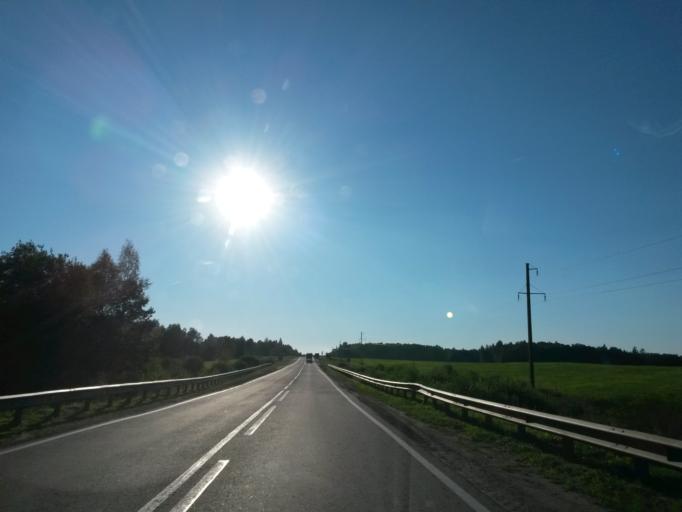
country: RU
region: Jaroslavl
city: Gavrilov-Yam
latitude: 57.2631
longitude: 40.0284
